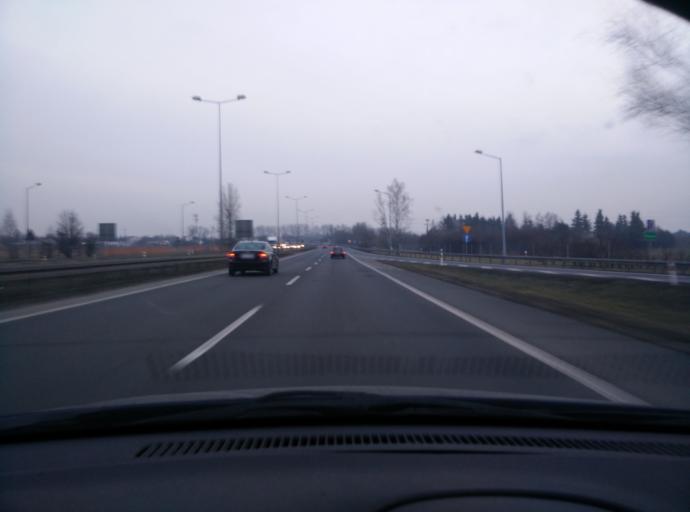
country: PL
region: Greater Poland Voivodeship
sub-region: Powiat poznanski
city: Daszewice
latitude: 52.3441
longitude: 16.9997
